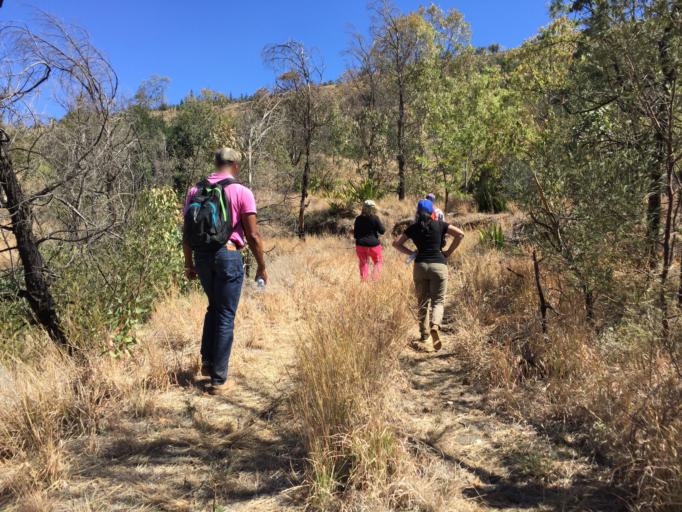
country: CV
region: Mosteiros
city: Porto dos Mosteiros
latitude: 15.0082
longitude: -24.3639
